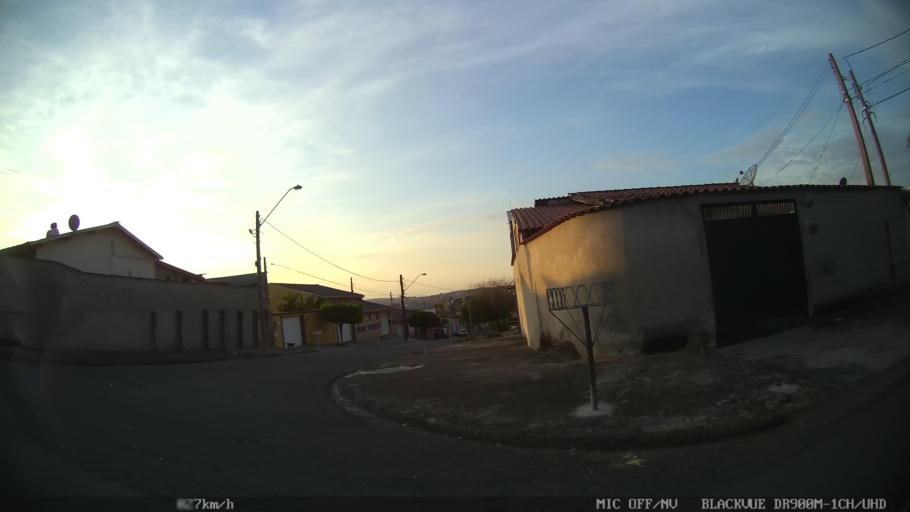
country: BR
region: Sao Paulo
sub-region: Campinas
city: Campinas
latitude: -22.9757
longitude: -47.1316
